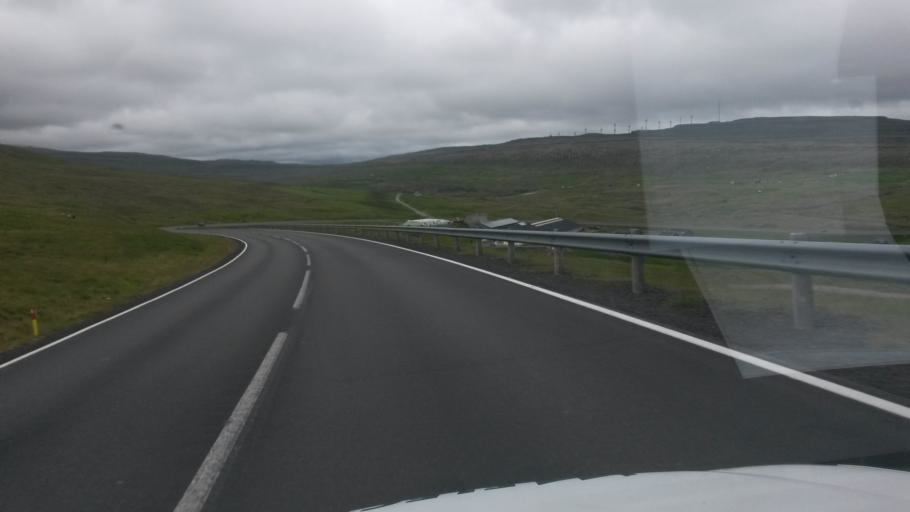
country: FO
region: Streymoy
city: Argir
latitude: 61.9973
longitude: -6.8439
